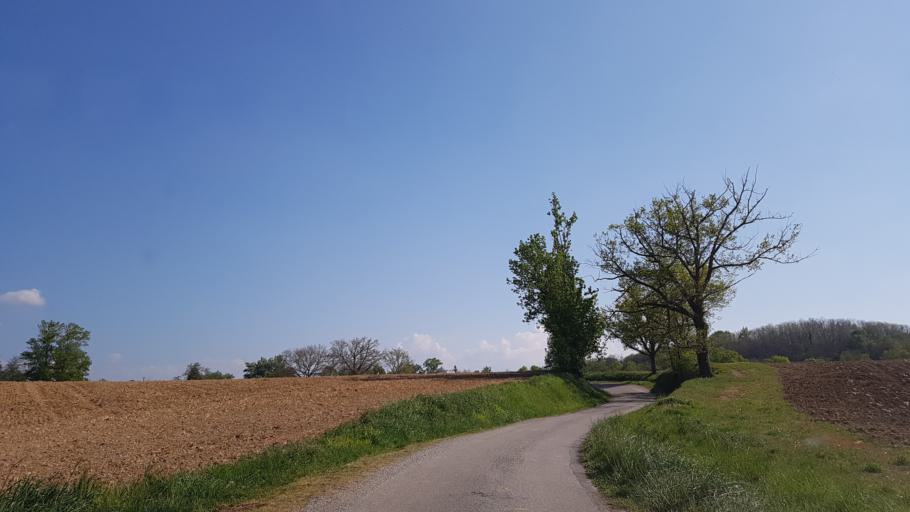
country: FR
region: Midi-Pyrenees
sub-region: Departement de l'Ariege
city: La Tour-du-Crieu
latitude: 43.0964
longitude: 1.7181
